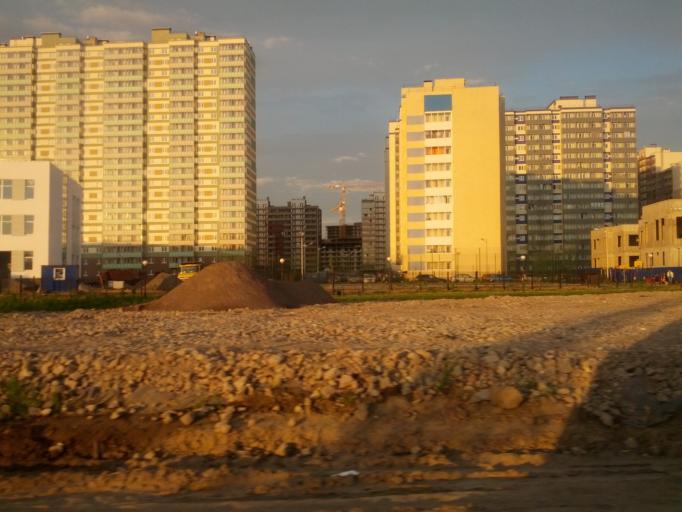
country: RU
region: Leningrad
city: Rybatskoye
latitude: 59.9020
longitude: 30.5055
